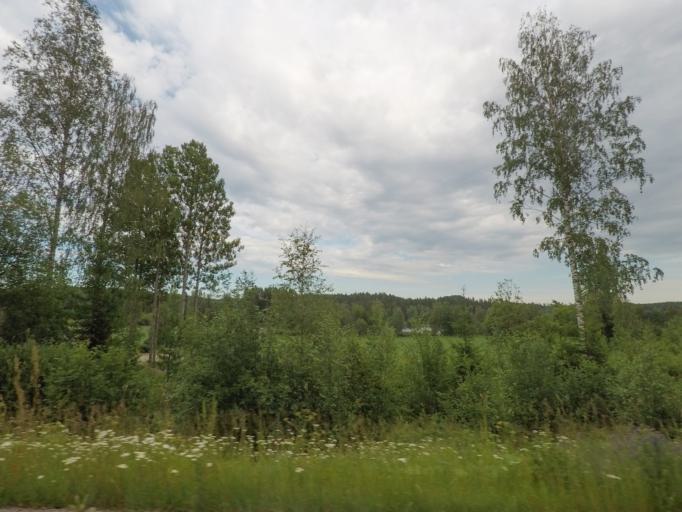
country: FI
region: Uusimaa
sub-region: Porvoo
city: Pukkila
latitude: 60.7643
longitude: 25.4450
